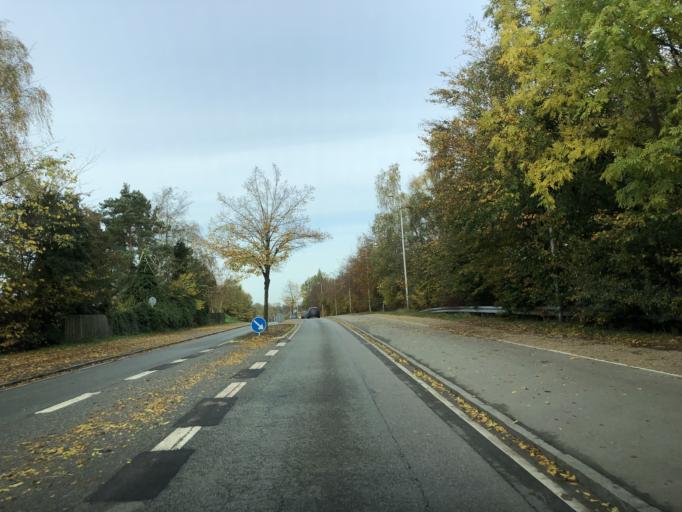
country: DK
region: Capital Region
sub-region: Rudersdal Kommune
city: Birkerod
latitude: 55.8504
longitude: 12.4224
